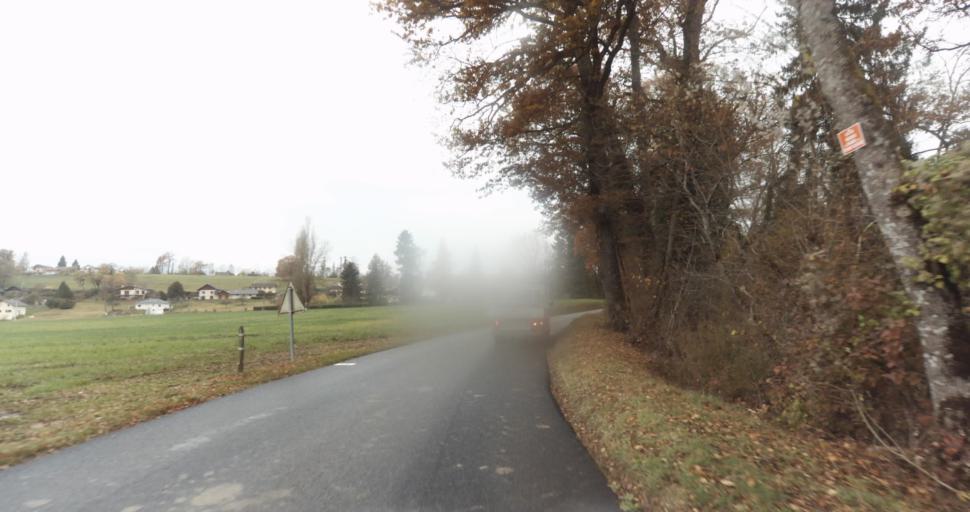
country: FR
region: Rhone-Alpes
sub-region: Departement de la Savoie
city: Albens
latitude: 45.7497
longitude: 5.9789
